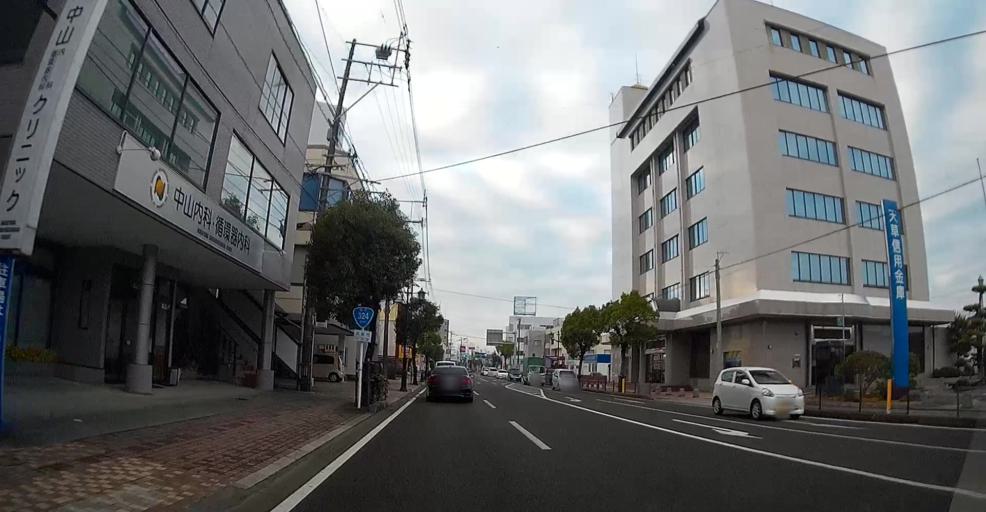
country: JP
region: Kumamoto
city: Hondo
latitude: 32.4510
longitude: 130.1975
